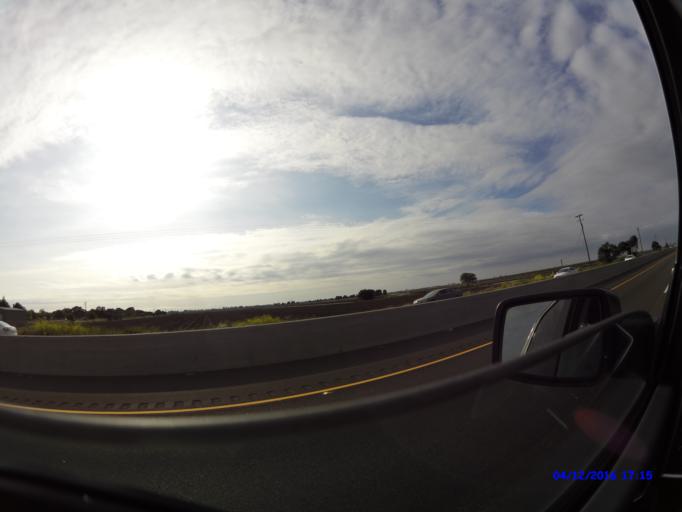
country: US
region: California
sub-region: San Joaquin County
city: French Camp
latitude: 37.8706
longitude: -121.2192
